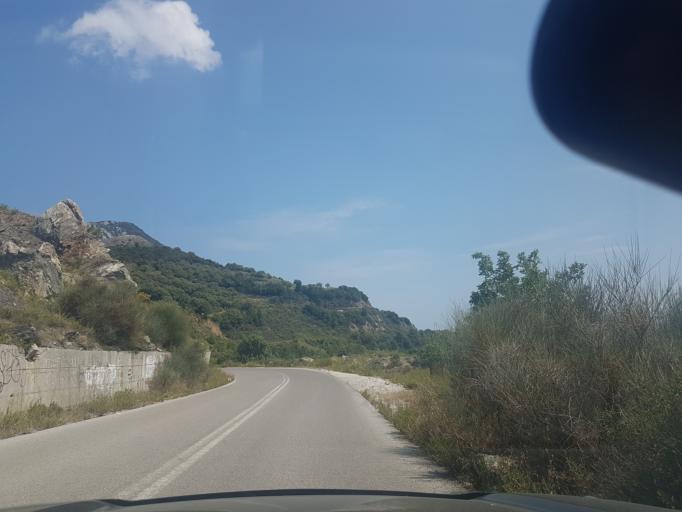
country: GR
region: Central Greece
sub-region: Nomos Evvoias
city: Yimnon
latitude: 38.6413
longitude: 23.8956
